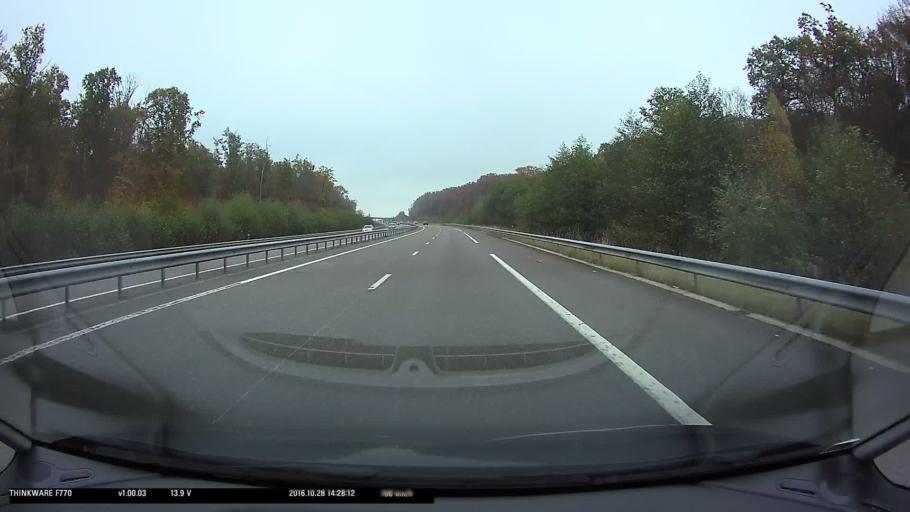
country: FR
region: Lorraine
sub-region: Departement de Meurthe-et-Moselle
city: Baccarat
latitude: 48.5848
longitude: 6.7921
